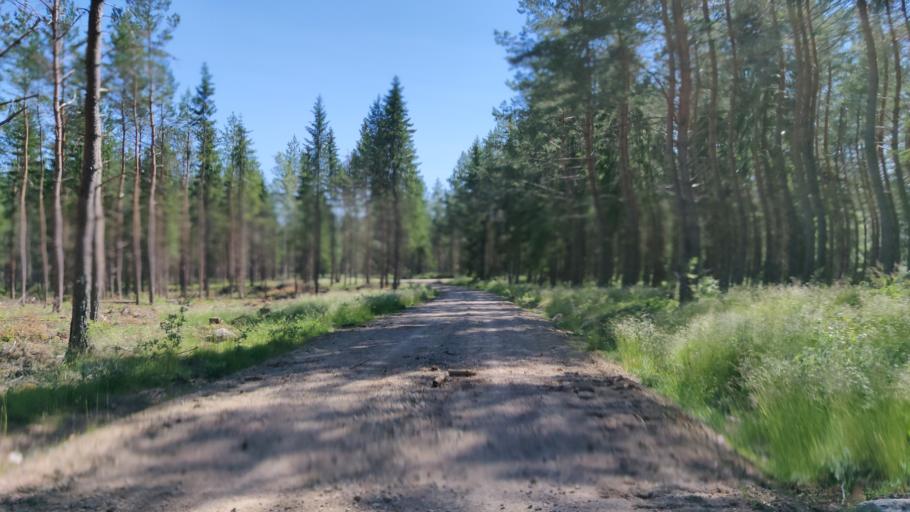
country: SE
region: Vaermland
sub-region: Hagfors Kommun
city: Hagfors
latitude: 59.9769
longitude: 13.6009
